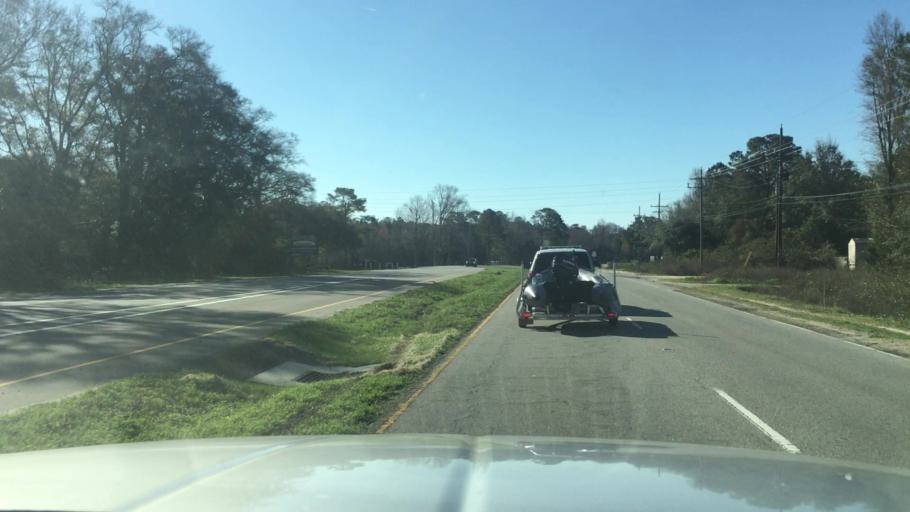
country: US
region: North Carolina
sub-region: New Hanover County
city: Sea Breeze
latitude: 34.0803
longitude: -77.8948
